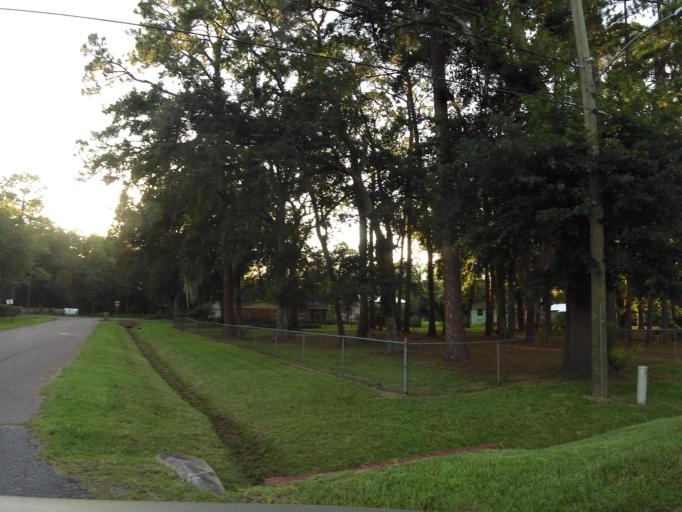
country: US
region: Florida
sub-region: Clay County
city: Bellair-Meadowbrook Terrace
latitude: 30.2390
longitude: -81.7376
